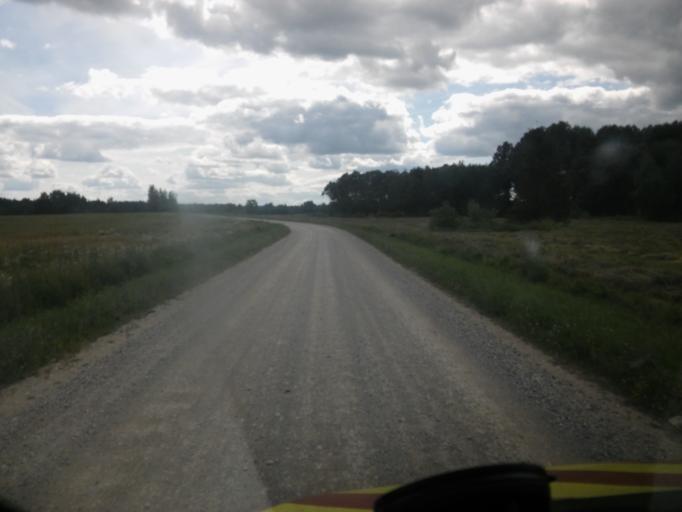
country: EE
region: Viljandimaa
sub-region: Karksi vald
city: Karksi-Nuia
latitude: 58.0955
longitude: 25.4940
